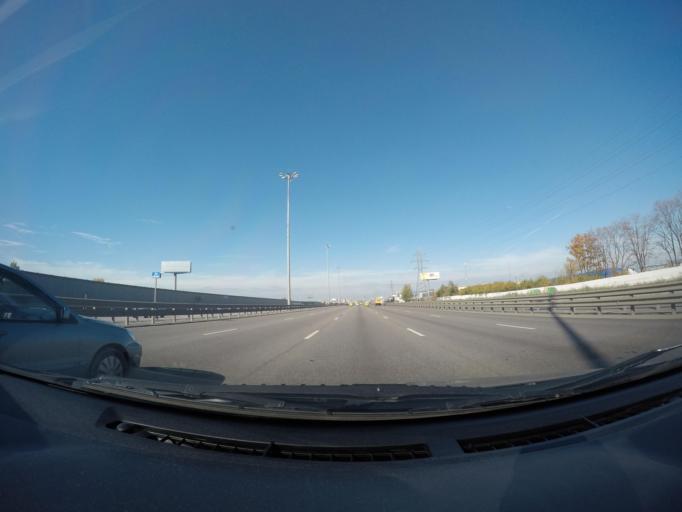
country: RU
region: Moskovskaya
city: Tomilino
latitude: 55.6462
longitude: 37.9135
